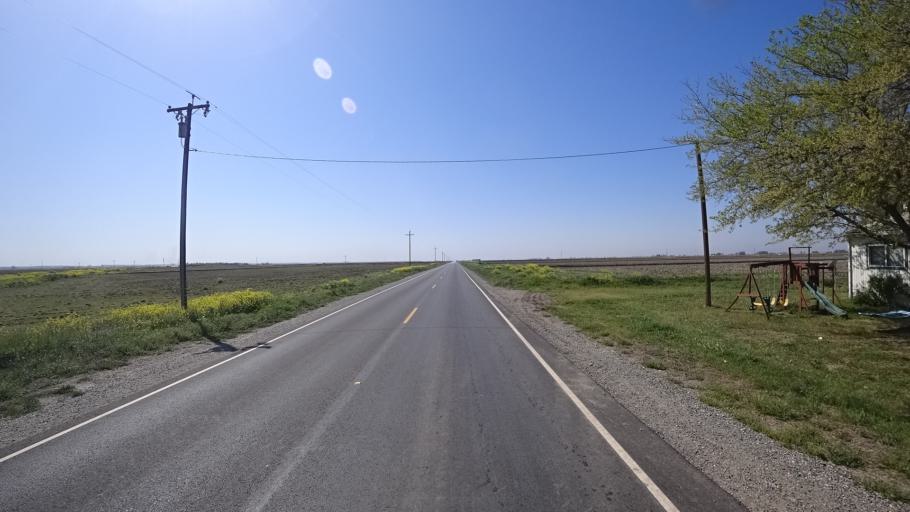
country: US
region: California
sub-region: Glenn County
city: Willows
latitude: 39.5614
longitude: -122.0652
